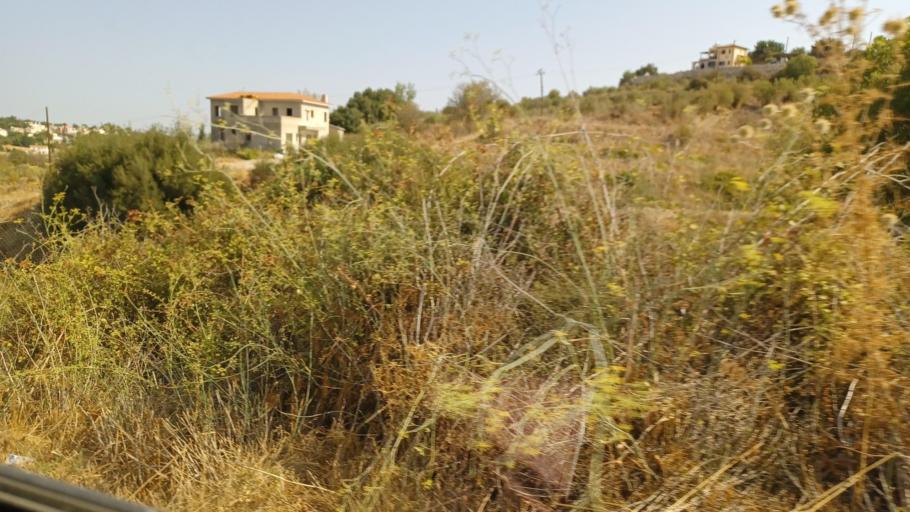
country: CY
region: Pafos
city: Tala
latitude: 34.9115
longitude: 32.4787
